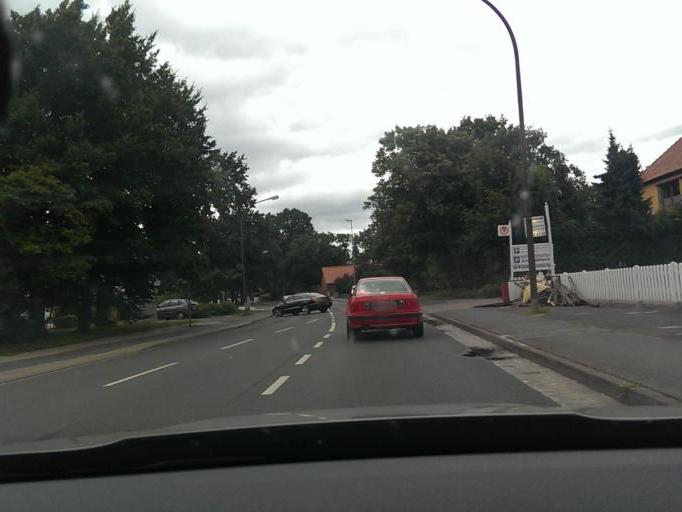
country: DE
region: Lower Saxony
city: Langenhagen
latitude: 52.4535
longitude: 9.7446
